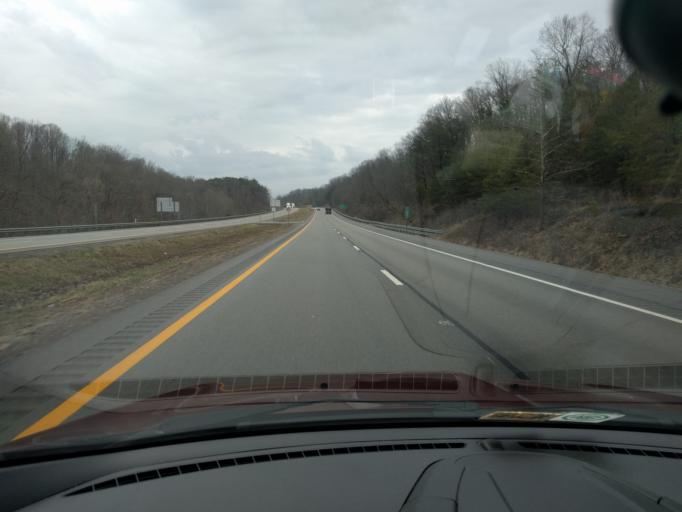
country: US
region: West Virginia
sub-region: Wood County
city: Boaz
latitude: 39.3204
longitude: -81.4717
